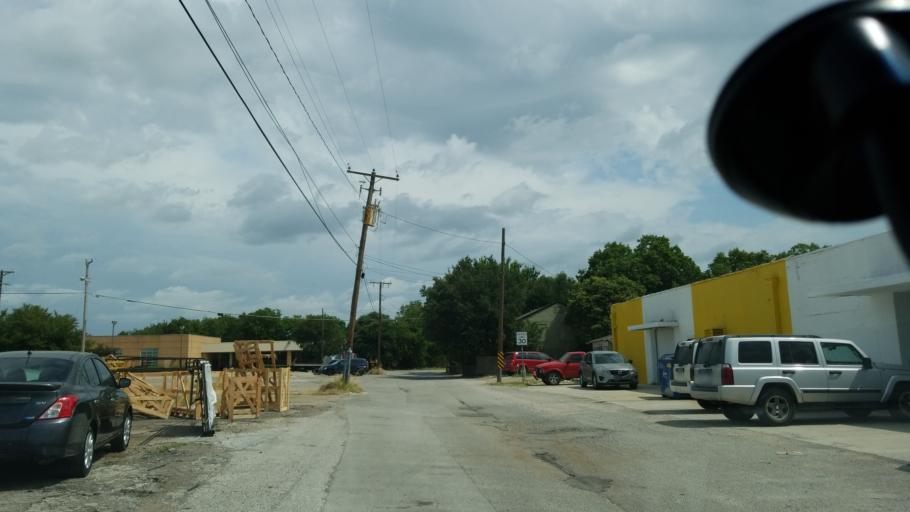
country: US
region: Texas
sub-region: Dallas County
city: Grand Prairie
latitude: 32.7470
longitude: -96.9935
